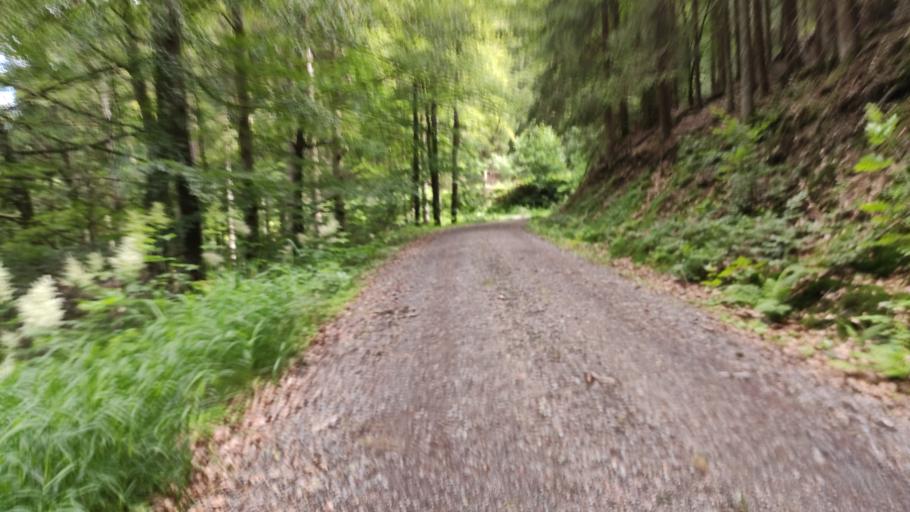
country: DE
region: Bavaria
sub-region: Upper Franconia
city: Tschirn
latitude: 50.3812
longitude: 11.4667
